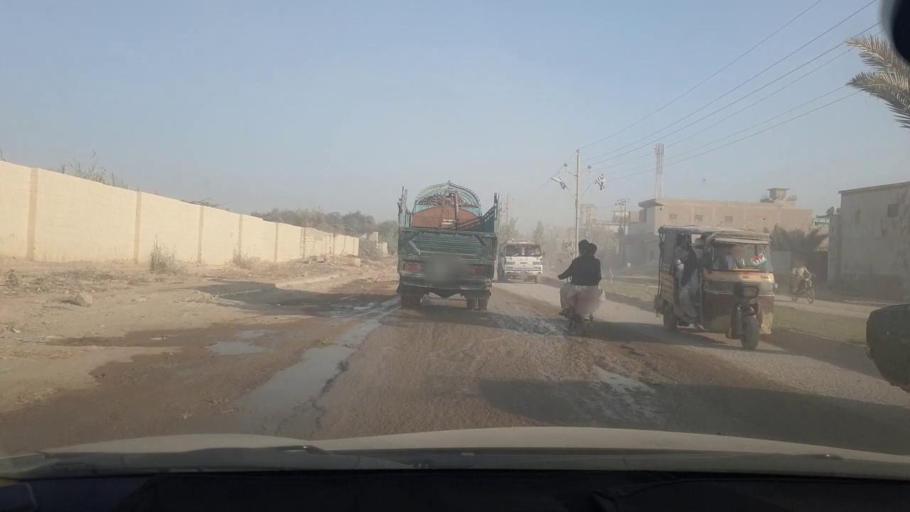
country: PK
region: Sindh
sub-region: Karachi District
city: Karachi
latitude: 24.9712
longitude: 67.0396
